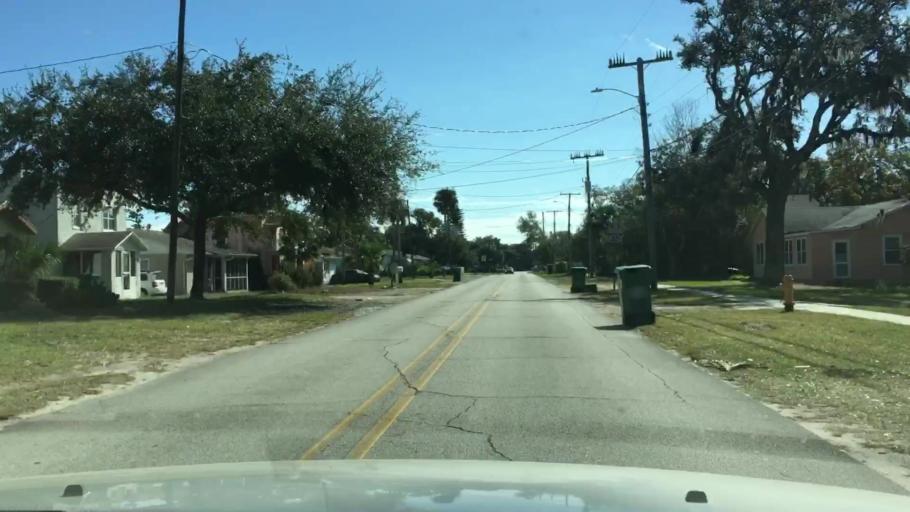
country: US
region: Florida
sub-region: Volusia County
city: Holly Hill
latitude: 29.2315
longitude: -81.0314
